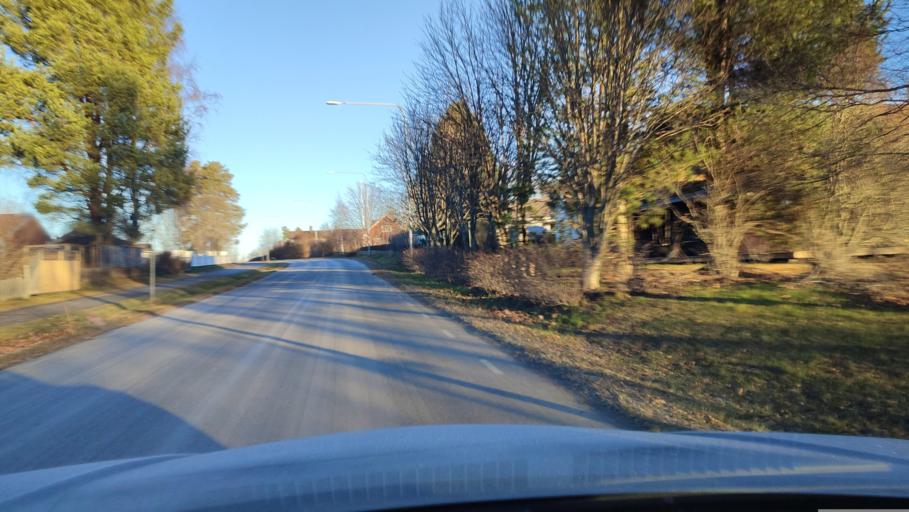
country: SE
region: Vaesterbotten
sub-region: Skelleftea Kommun
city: Viken
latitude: 64.7430
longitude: 20.9198
